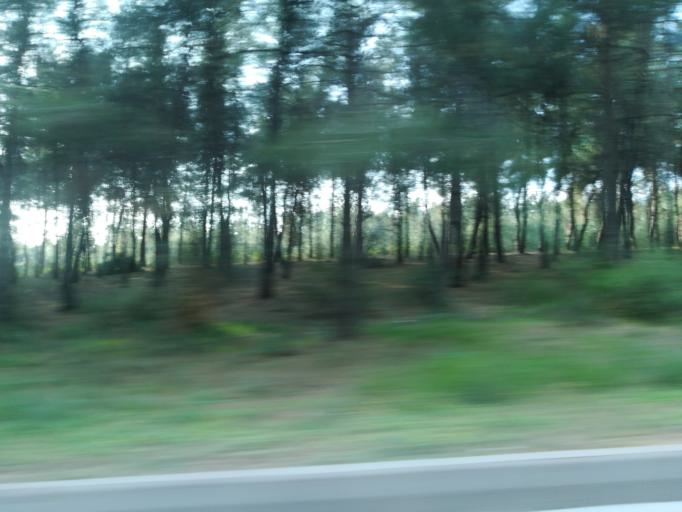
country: TR
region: Adana
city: Adana
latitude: 37.0391
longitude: 35.3529
